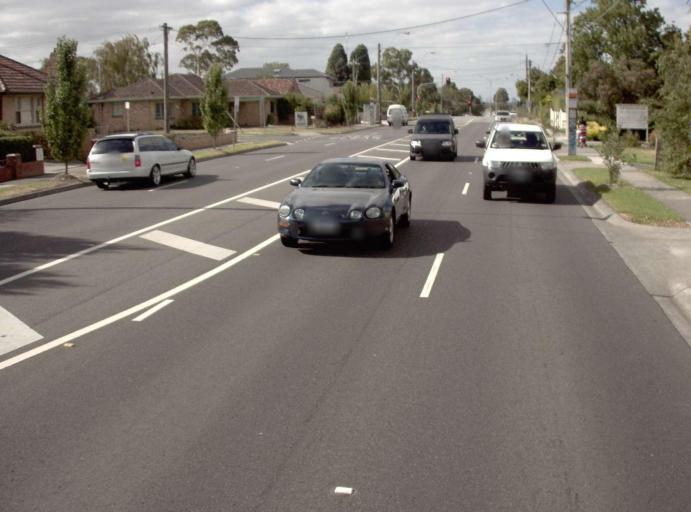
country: AU
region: Victoria
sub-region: Greater Dandenong
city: Dandenong North
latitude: -37.9792
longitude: 145.2219
